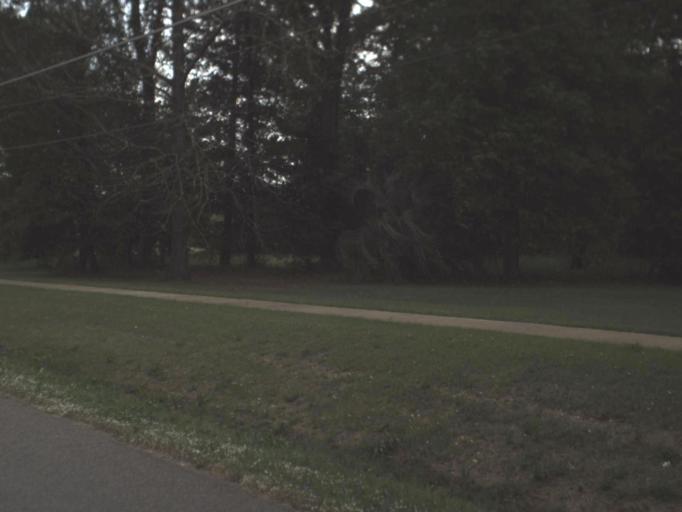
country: US
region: Florida
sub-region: Escambia County
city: Century
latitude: 30.9428
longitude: -87.1554
